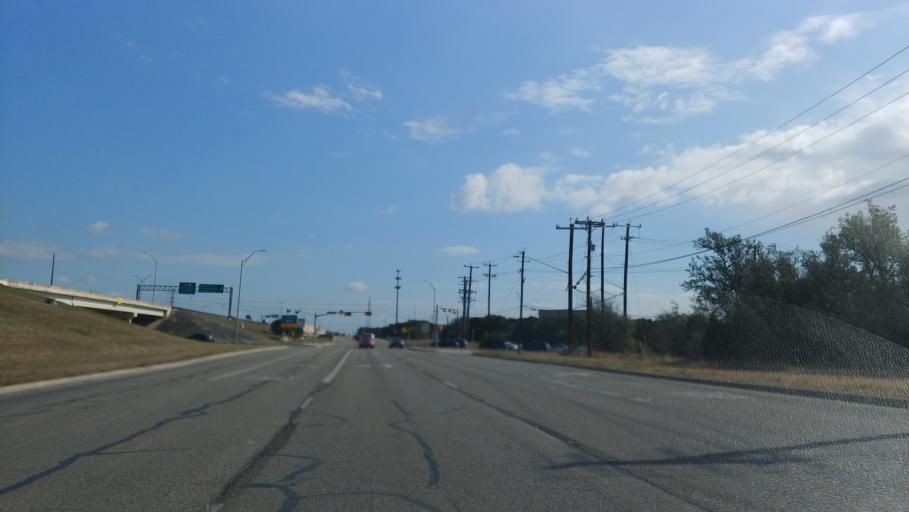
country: US
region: Texas
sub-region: Bexar County
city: Helotes
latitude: 29.5863
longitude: -98.6328
